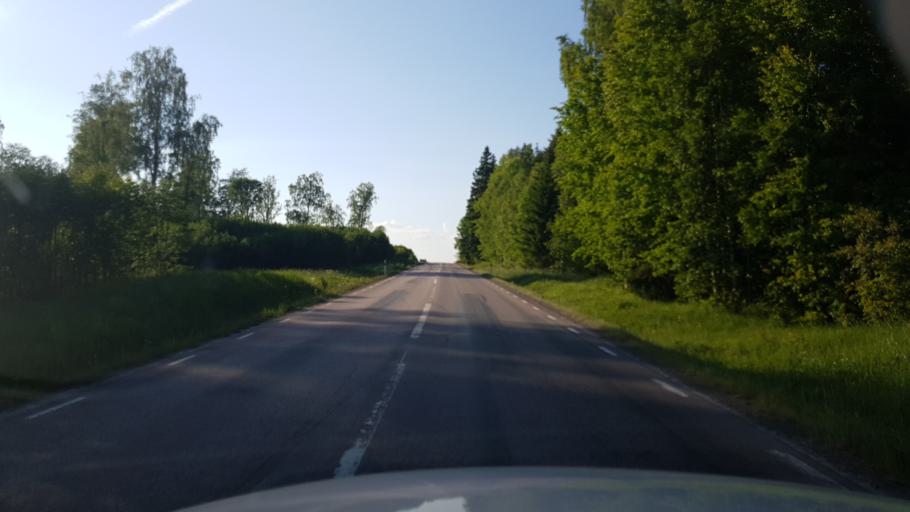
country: SE
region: Vaestmanland
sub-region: Kopings Kommun
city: Kolsva
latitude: 59.6147
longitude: 15.8259
